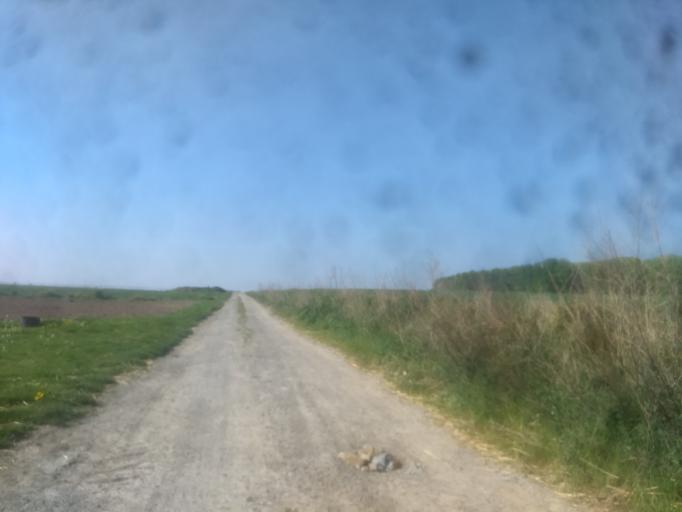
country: FR
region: Nord-Pas-de-Calais
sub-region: Departement du Pas-de-Calais
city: Beaurains
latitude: 50.2631
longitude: 2.8066
